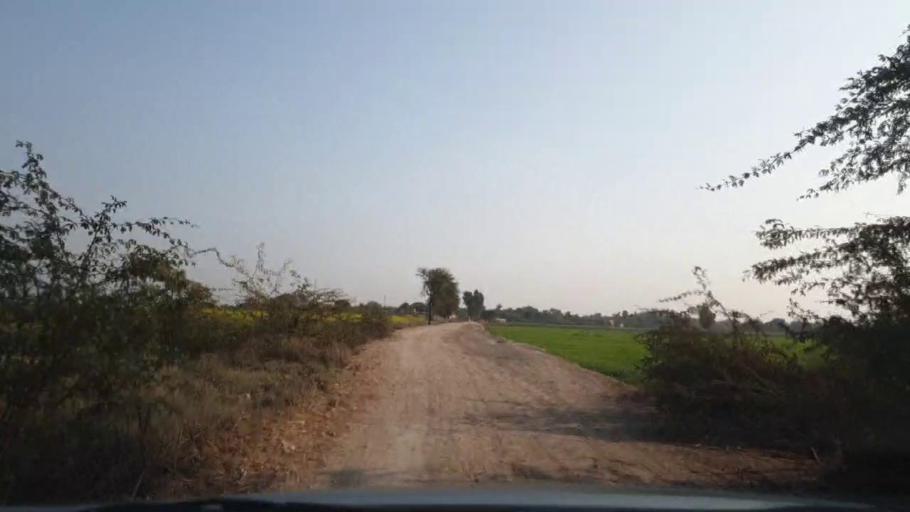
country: PK
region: Sindh
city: Tando Adam
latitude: 25.6678
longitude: 68.6478
